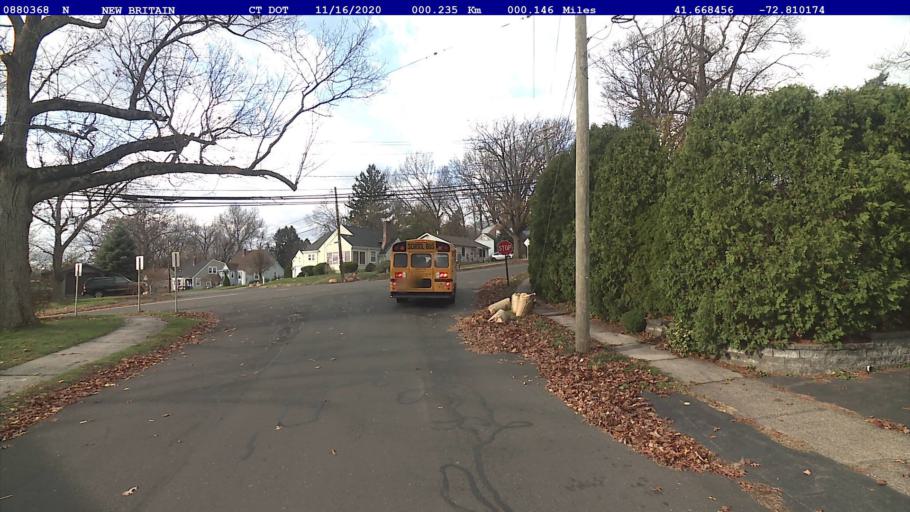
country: US
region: Connecticut
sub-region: Hartford County
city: New Britain
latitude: 41.6685
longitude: -72.8102
